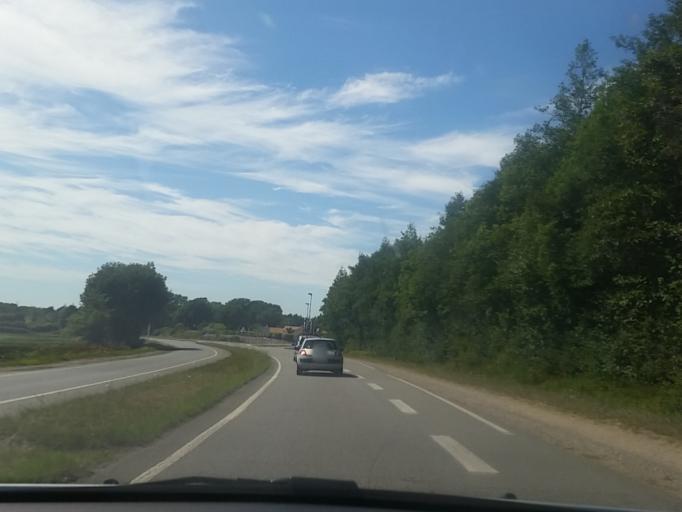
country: FR
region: Pays de la Loire
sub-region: Departement de la Loire-Atlantique
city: Saint-Pere-en-Retz
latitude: 47.2003
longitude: -2.0358
